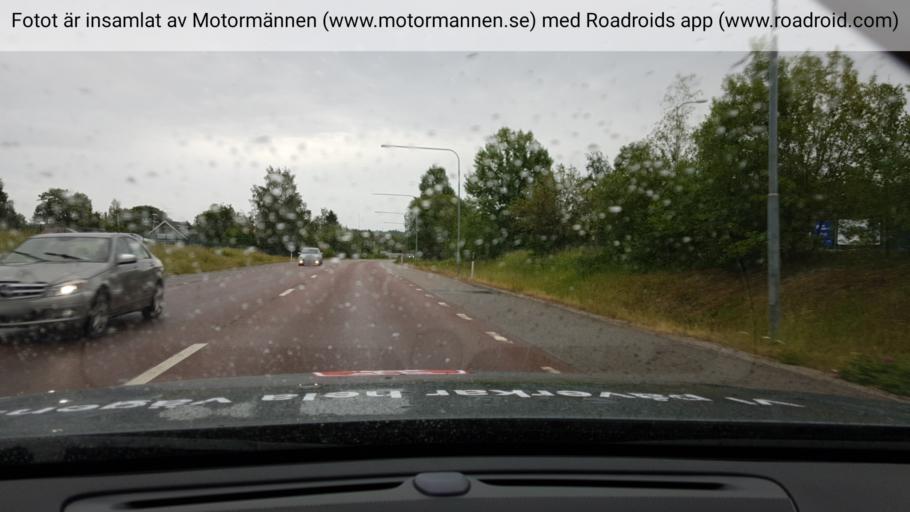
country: SE
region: Stockholm
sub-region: Vallentuna Kommun
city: Vallentuna
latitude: 59.5341
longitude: 18.0662
